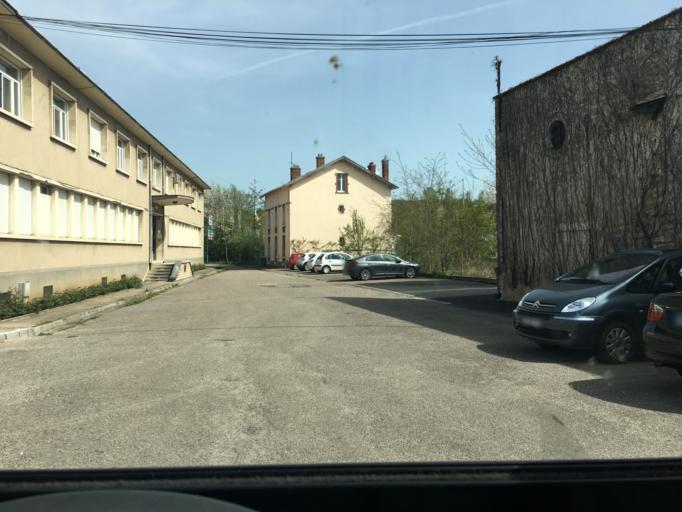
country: FR
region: Lorraine
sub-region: Departement de Meurthe-et-Moselle
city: Saint-Nicolas-de-Port
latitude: 48.6340
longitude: 6.3056
